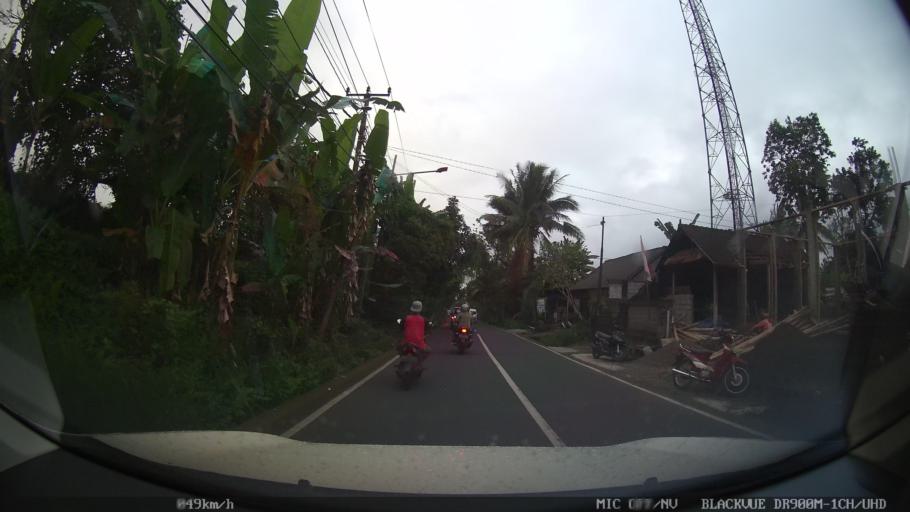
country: ID
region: Bali
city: Badung
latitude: -8.4190
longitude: 115.2453
